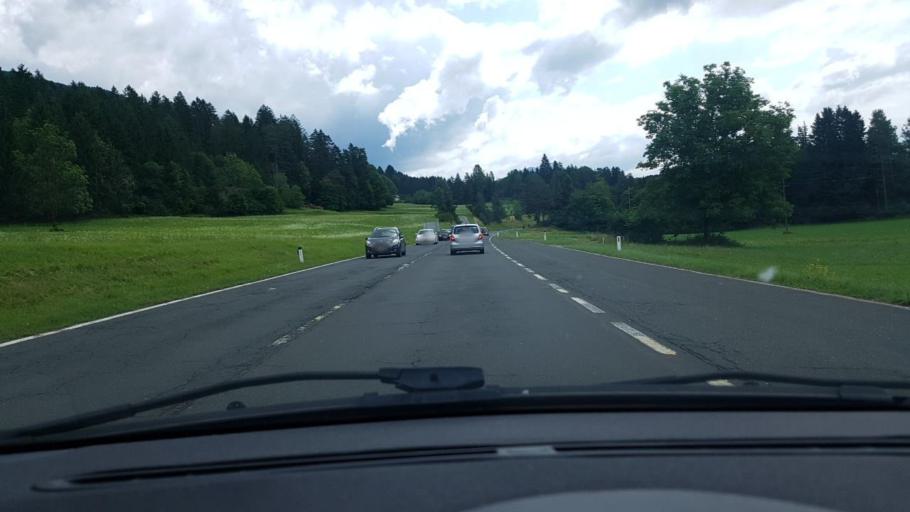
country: AT
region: Carinthia
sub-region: Politischer Bezirk Villach Land
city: Stockenboi
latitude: 46.6283
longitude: 13.4773
